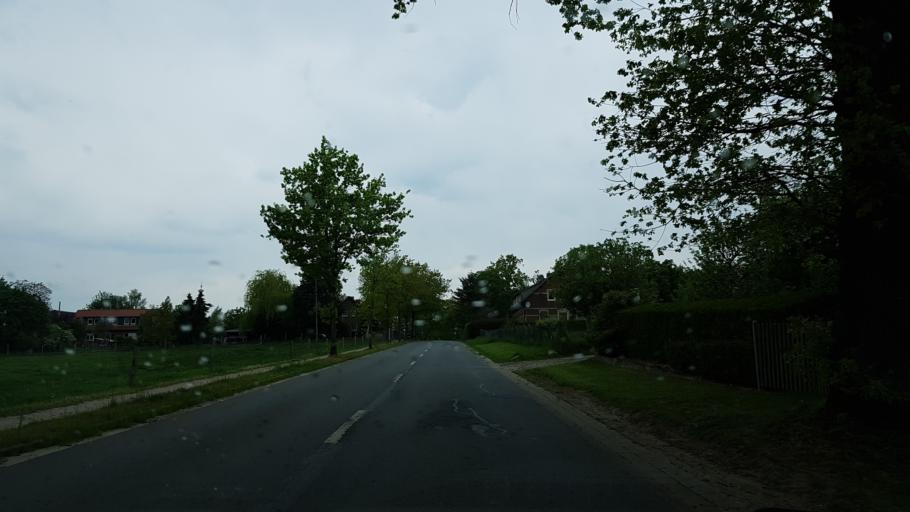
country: DE
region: Lower Saxony
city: Gartow
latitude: 53.0552
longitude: 11.4309
